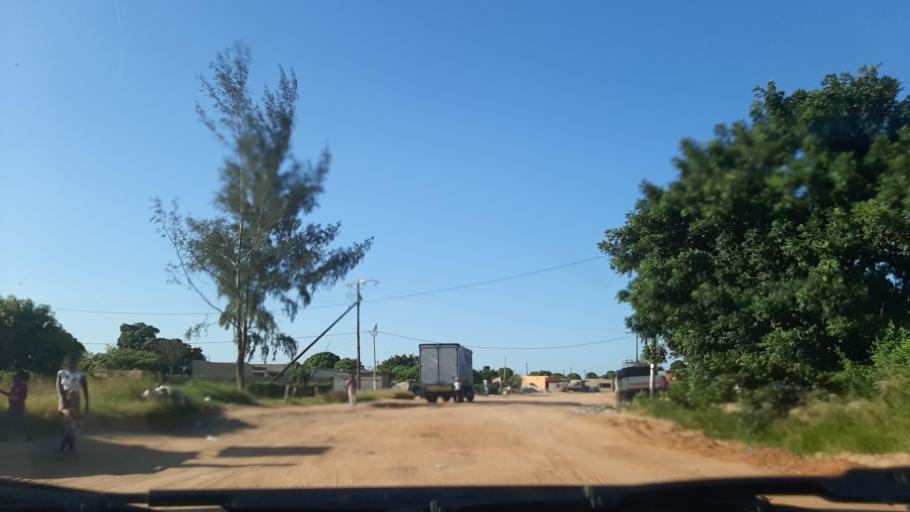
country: MZ
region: Maputo City
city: Maputo
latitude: -25.8039
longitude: 32.5470
